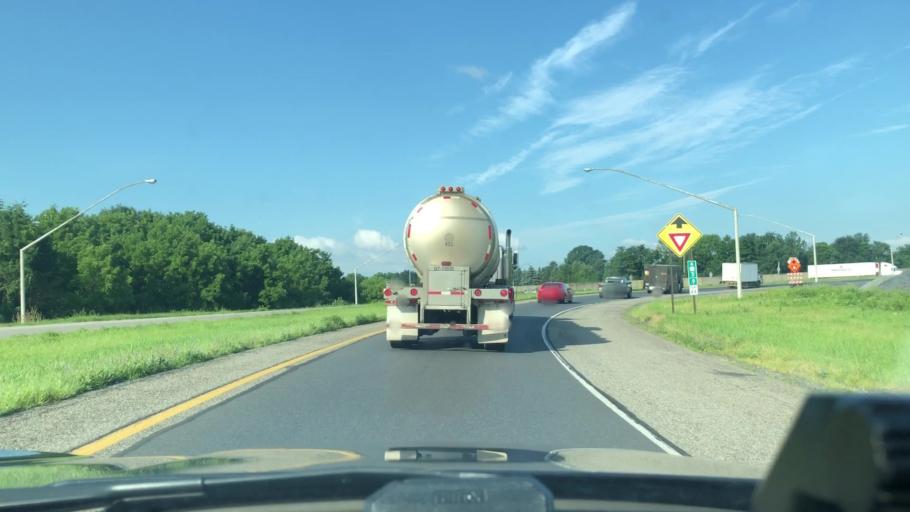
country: US
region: Pennsylvania
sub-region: Northampton County
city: Palmer Heights
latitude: 40.6810
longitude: -75.2862
